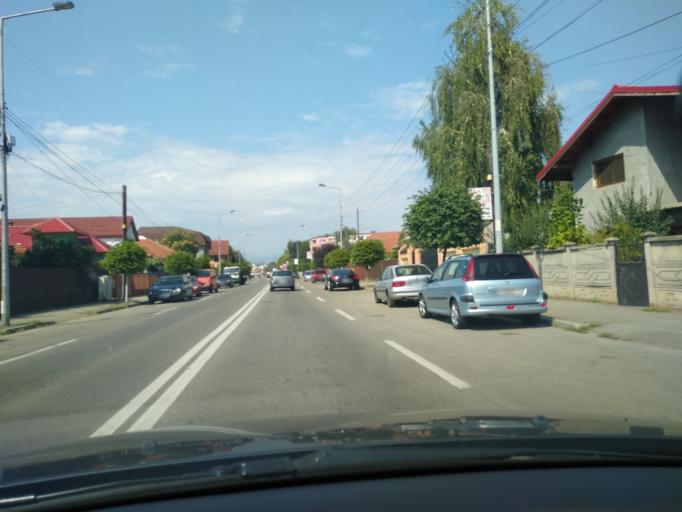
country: RO
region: Gorj
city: Targu Jiu
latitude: 45.0212
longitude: 23.2684
